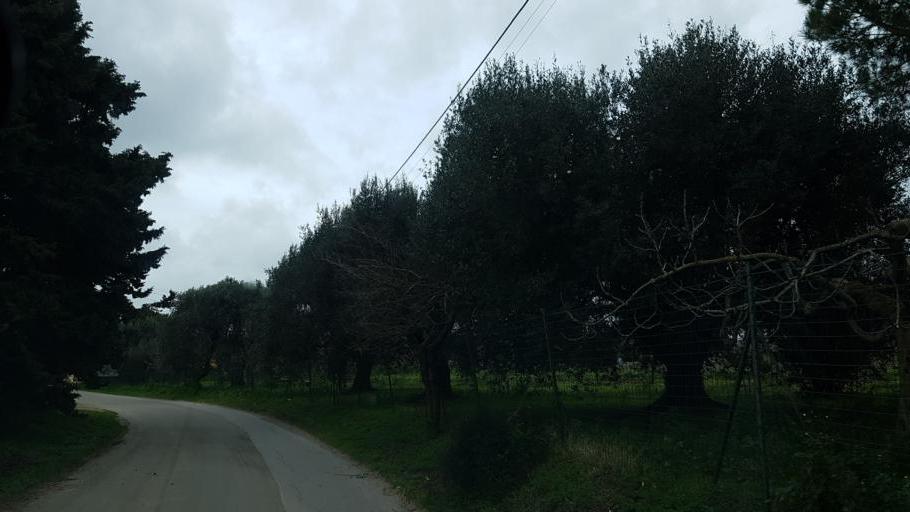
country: IT
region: Apulia
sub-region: Provincia di Brindisi
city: La Rosa
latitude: 40.6057
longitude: 17.9247
